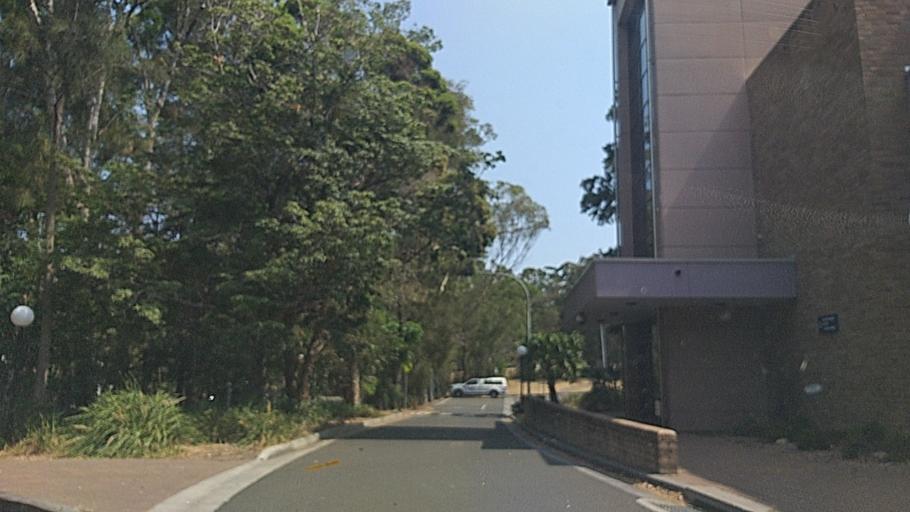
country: AU
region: New South Wales
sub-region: Wollongong
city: Mount Ousley
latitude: -34.4062
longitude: 150.8772
